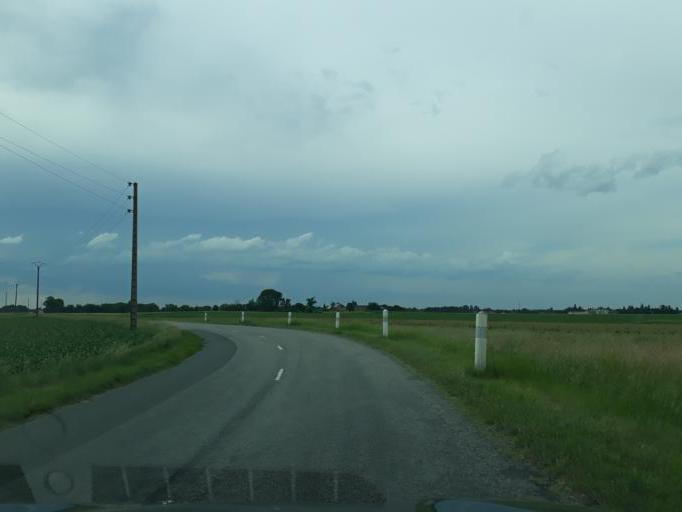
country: FR
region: Centre
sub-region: Departement du Loiret
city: Vienne-en-Val
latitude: 47.8212
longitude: 2.1621
